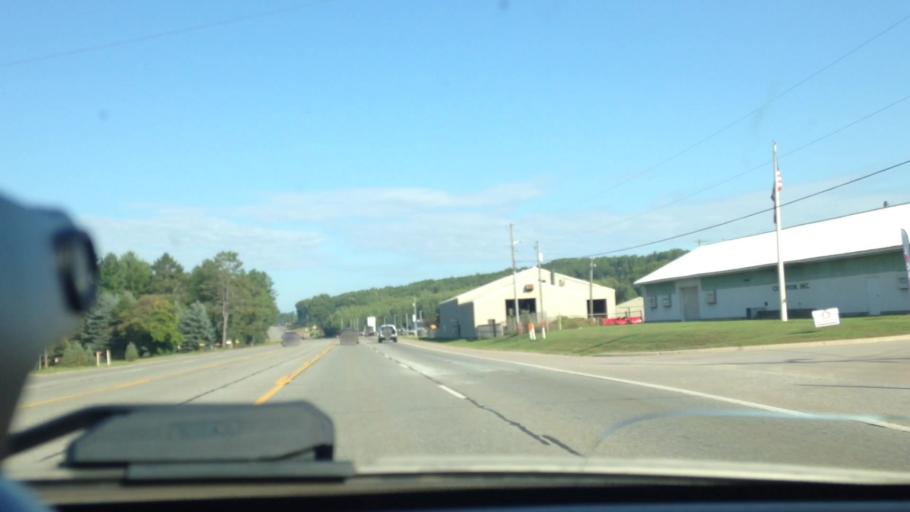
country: US
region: Michigan
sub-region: Dickinson County
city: Iron Mountain
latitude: 45.8487
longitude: -88.0515
